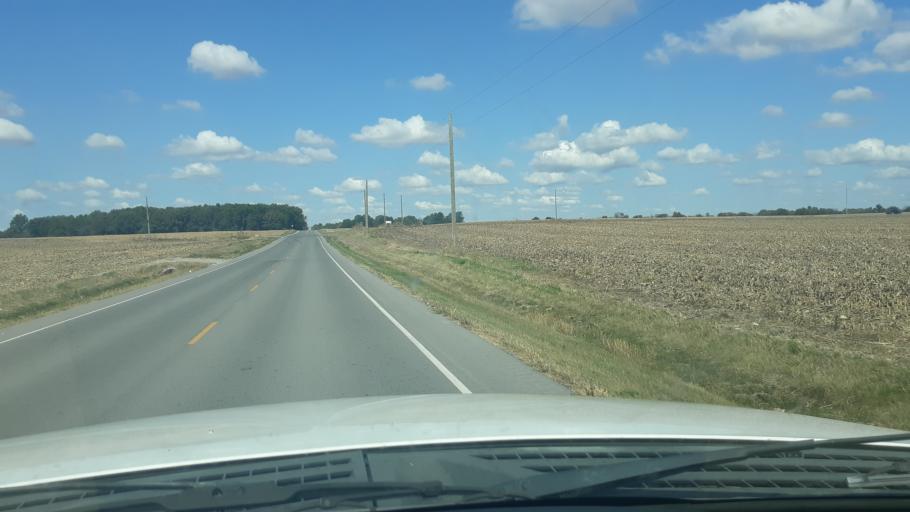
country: US
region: Illinois
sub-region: Saline County
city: Eldorado
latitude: 37.8027
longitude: -88.4847
